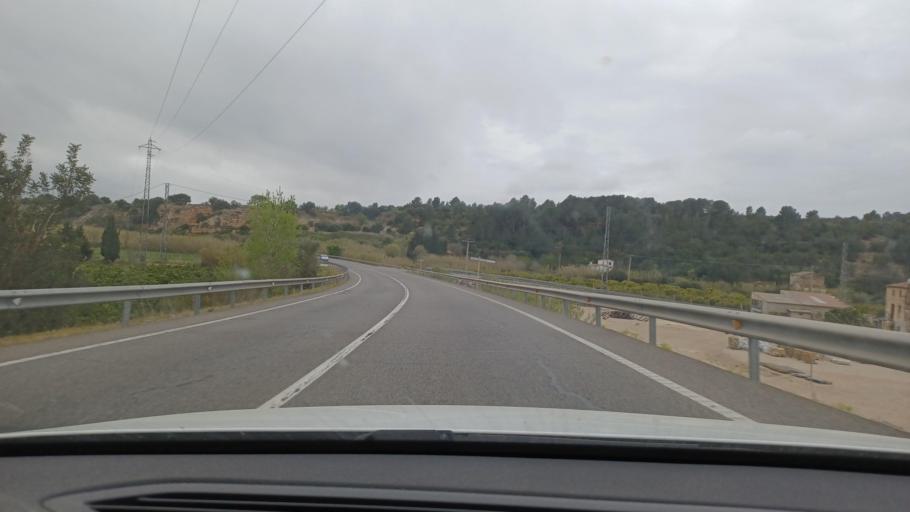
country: ES
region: Catalonia
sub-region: Provincia de Tarragona
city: Tortosa
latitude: 40.7906
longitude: 0.4960
